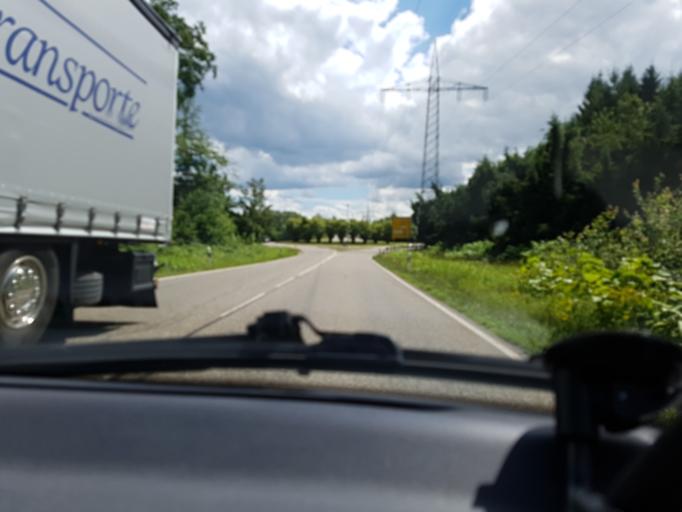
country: DE
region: Baden-Wuerttemberg
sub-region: Freiburg Region
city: Offenburg
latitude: 48.4729
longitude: 7.9210
